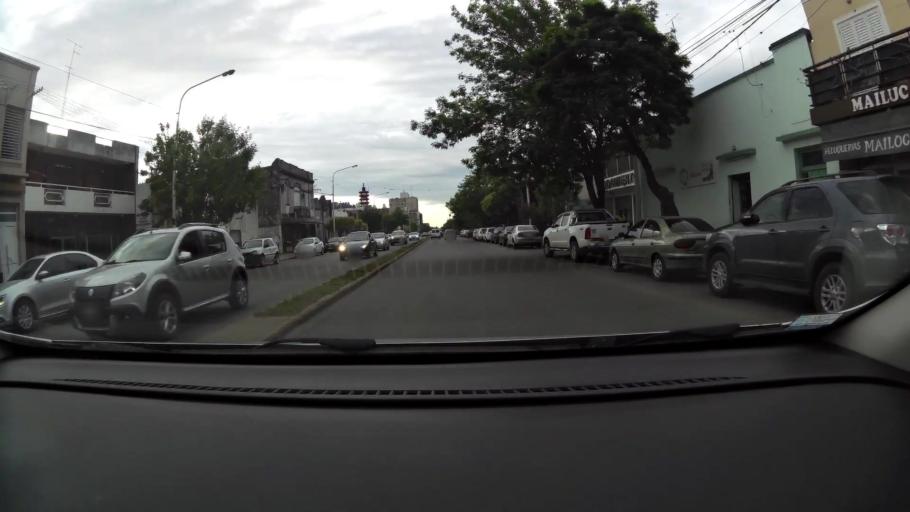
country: AR
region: Buenos Aires
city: San Nicolas de los Arroyos
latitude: -33.3394
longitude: -60.2180
